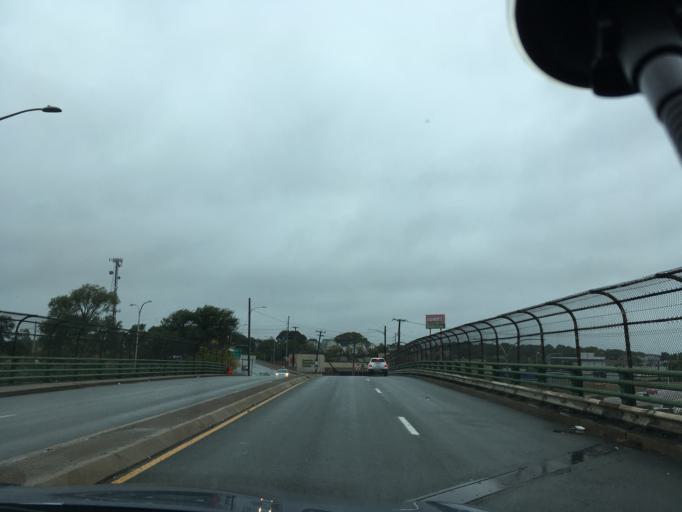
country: US
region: Rhode Island
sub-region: Providence County
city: Providence
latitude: 41.8457
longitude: -71.4107
